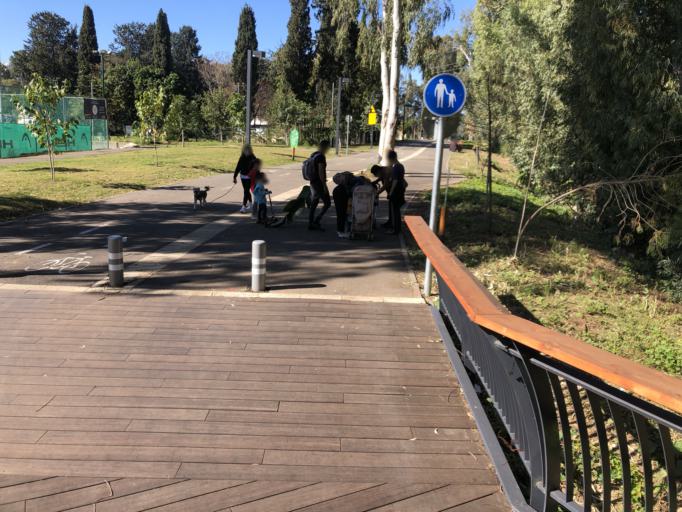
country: IL
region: Tel Aviv
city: Ramat Gan
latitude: 32.0977
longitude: 34.8174
